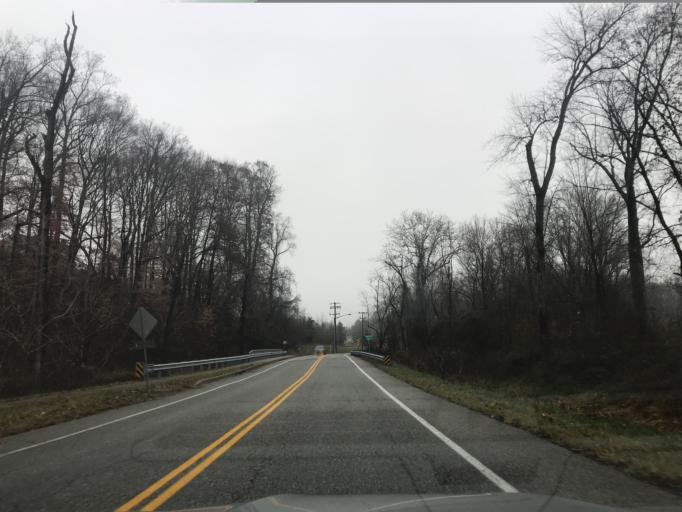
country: US
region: Maryland
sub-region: Harford County
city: South Bel Air
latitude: 39.5496
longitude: -76.3346
